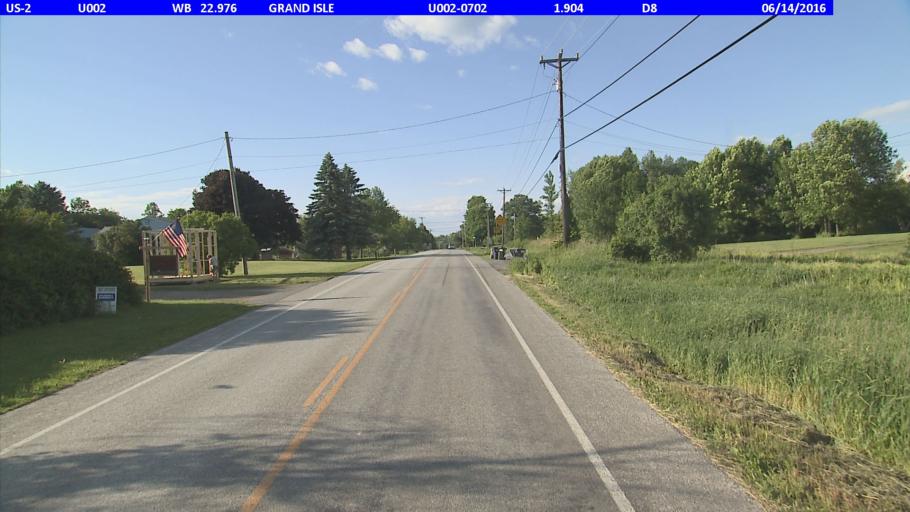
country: US
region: Vermont
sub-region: Grand Isle County
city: North Hero
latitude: 44.7400
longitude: -73.2897
